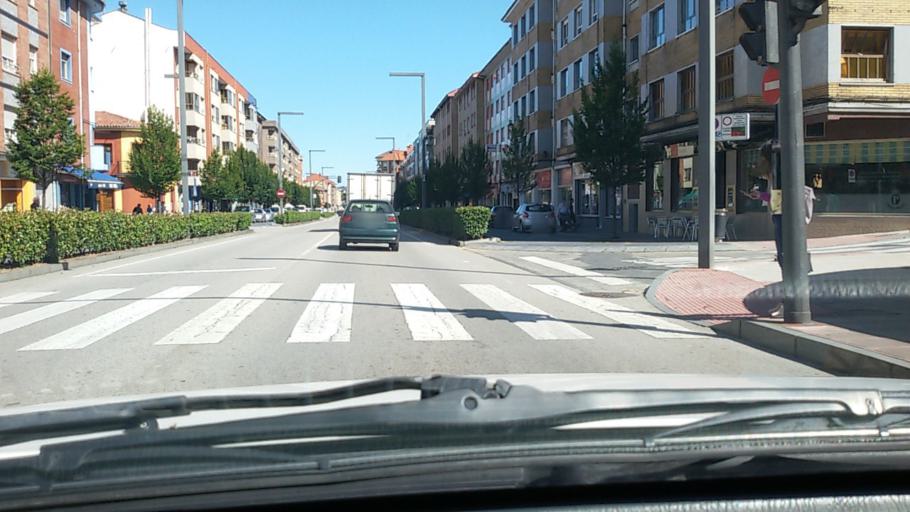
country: ES
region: Asturias
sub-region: Province of Asturias
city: Lugones
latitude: 43.4014
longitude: -5.8102
